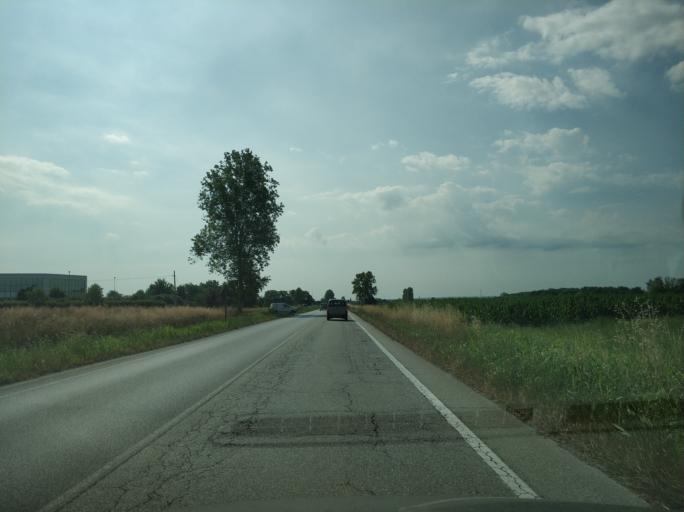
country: IT
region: Piedmont
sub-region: Provincia di Torino
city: Marocchi
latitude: 44.9500
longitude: 7.8010
